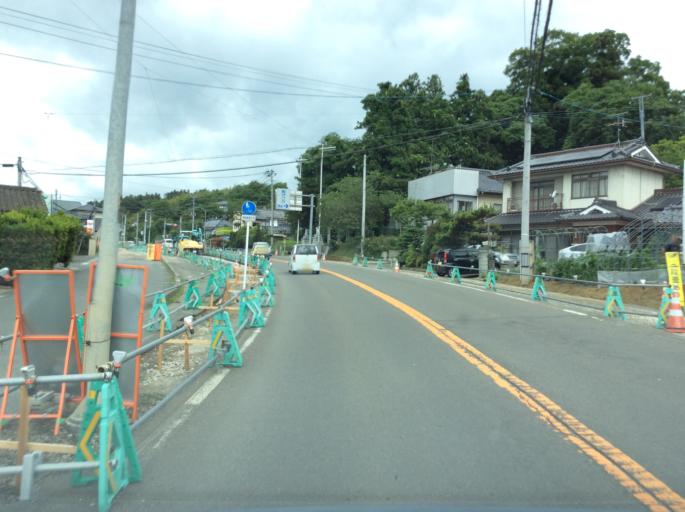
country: JP
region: Fukushima
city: Fukushima-shi
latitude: 37.6821
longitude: 140.5639
